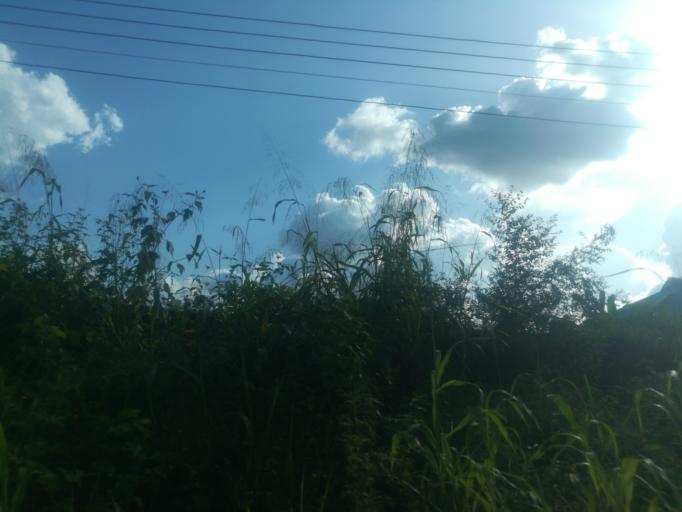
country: NG
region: Oyo
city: Ibadan
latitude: 7.4343
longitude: 3.9760
